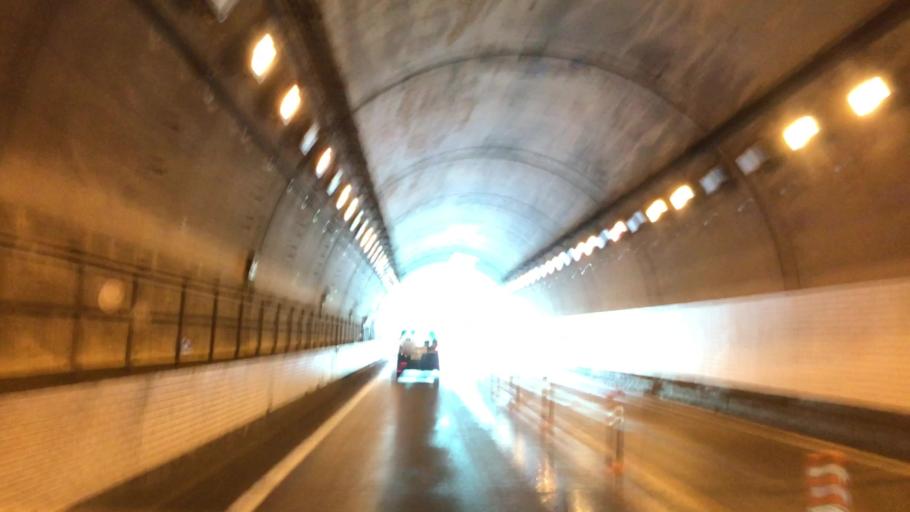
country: JP
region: Hokkaido
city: Muroran
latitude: 42.3891
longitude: 141.0464
